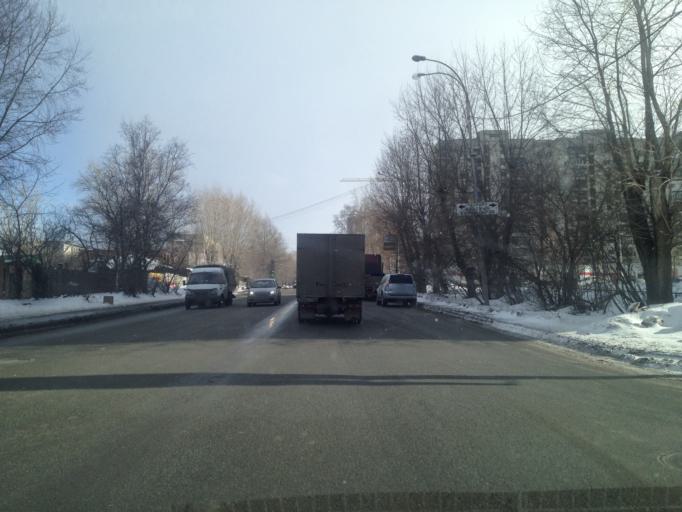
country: RU
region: Sverdlovsk
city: Yekaterinburg
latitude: 56.8987
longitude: 60.6290
